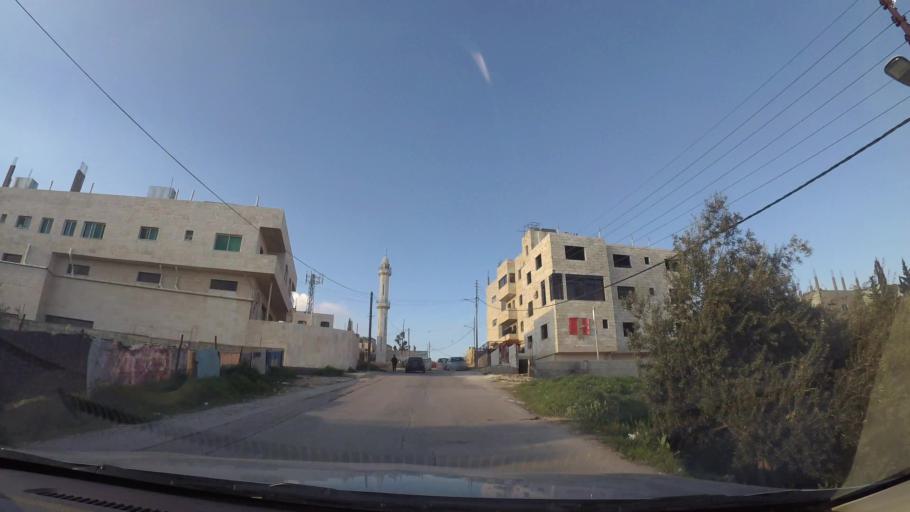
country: JO
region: Amman
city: Al Bunayyat ash Shamaliyah
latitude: 31.9044
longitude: 35.9079
